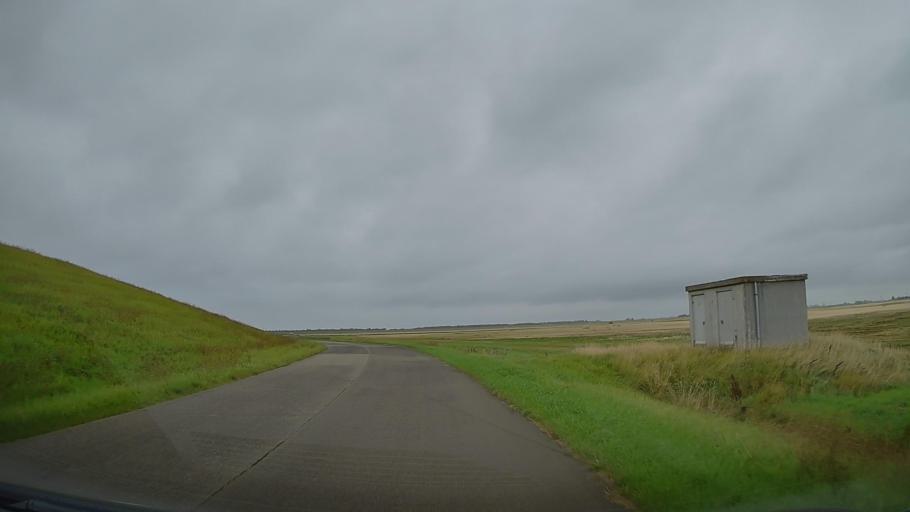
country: DE
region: Schleswig-Holstein
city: Busenwurth
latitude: 54.0588
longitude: 8.9877
